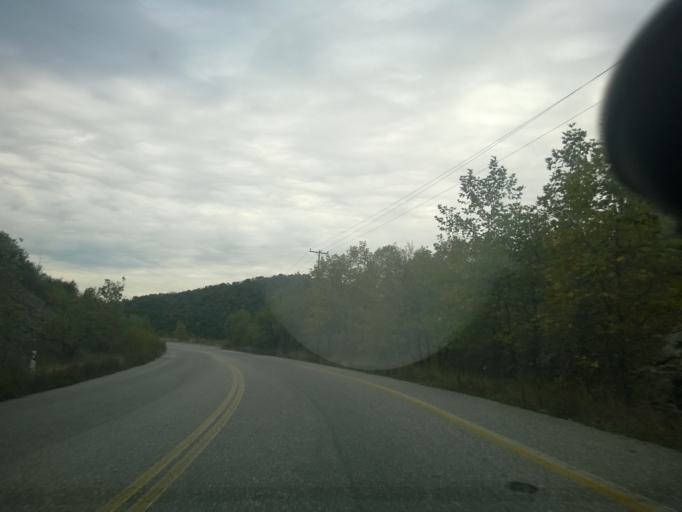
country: GR
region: Central Macedonia
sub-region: Nomos Pellis
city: Profitis Ilias
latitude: 40.8372
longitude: 22.1182
